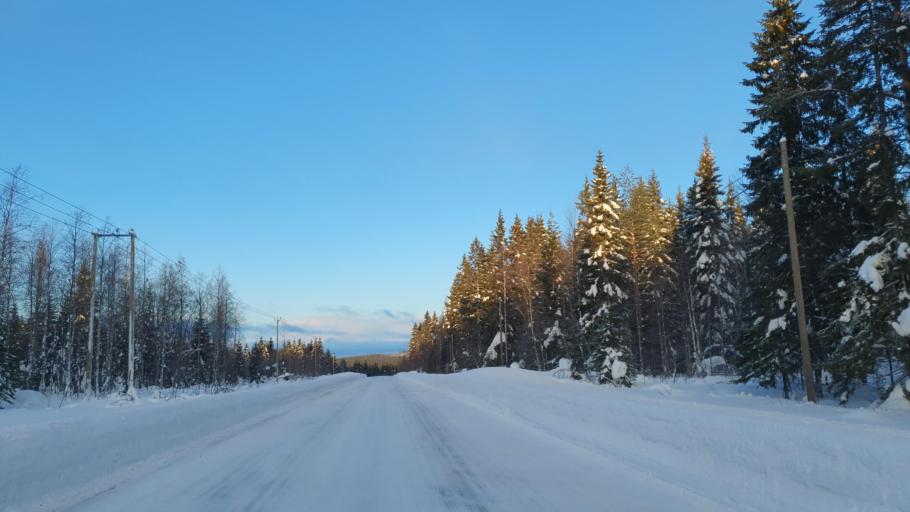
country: FI
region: Kainuu
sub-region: Kajaani
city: Ristijaervi
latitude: 64.3371
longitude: 28.0697
